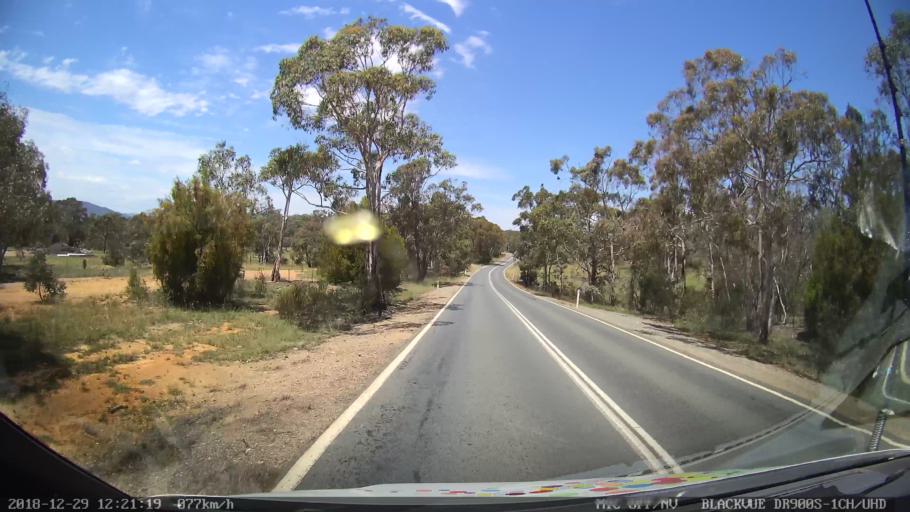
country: AU
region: New South Wales
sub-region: Queanbeyan
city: Queanbeyan
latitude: -35.4123
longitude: 149.2243
